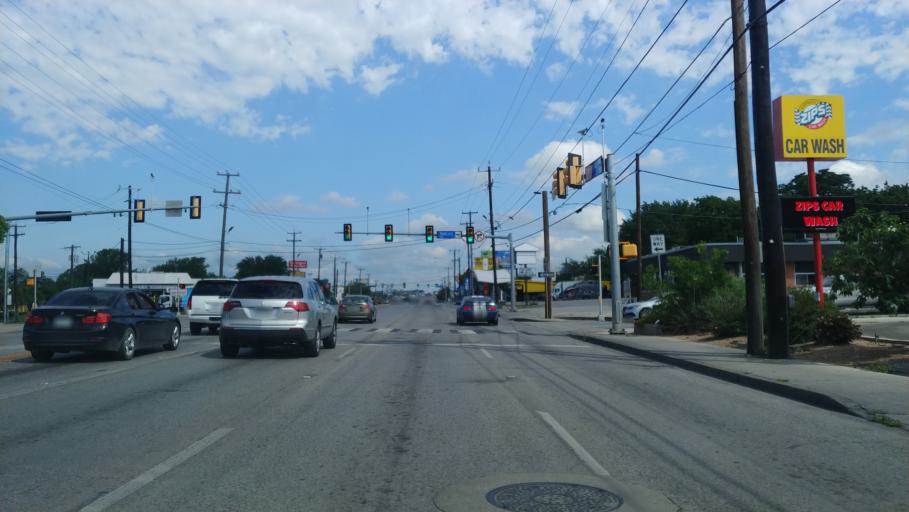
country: US
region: Texas
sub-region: Bexar County
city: Balcones Heights
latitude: 29.4718
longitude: -98.5332
